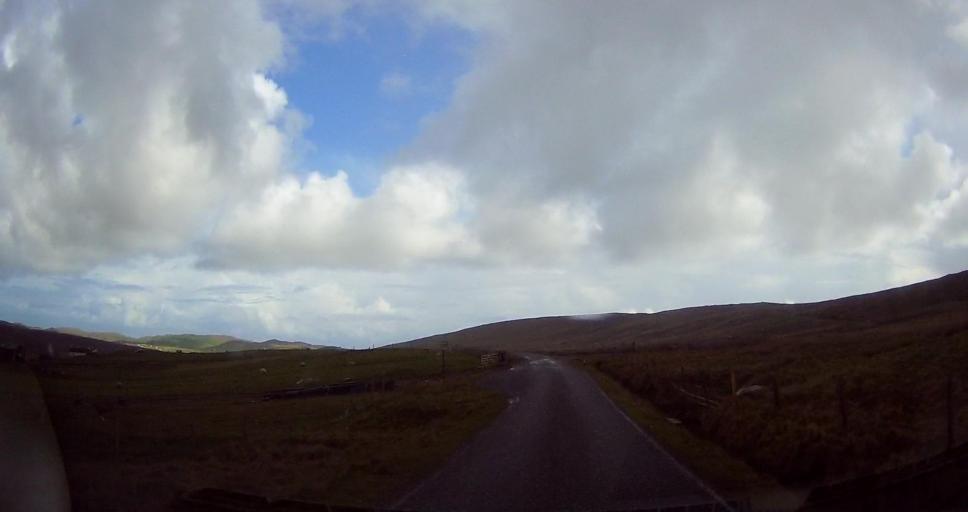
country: GB
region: Scotland
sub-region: Shetland Islands
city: Lerwick
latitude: 60.5589
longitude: -1.3381
